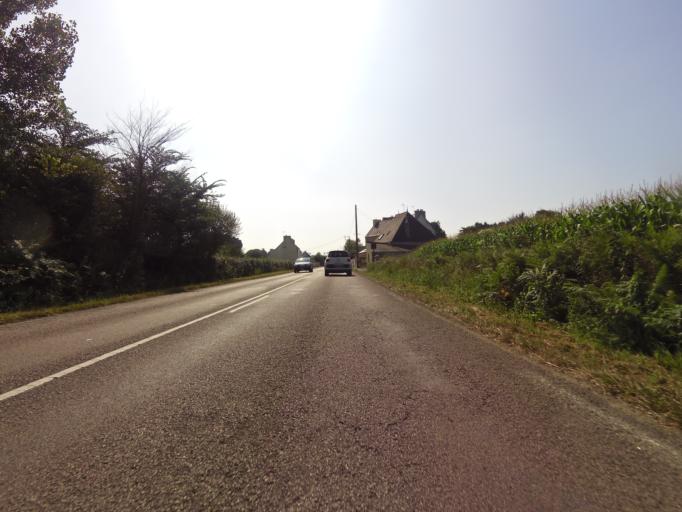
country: FR
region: Brittany
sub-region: Departement du Finistere
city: Plouhinec
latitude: 48.0069
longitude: -4.4560
